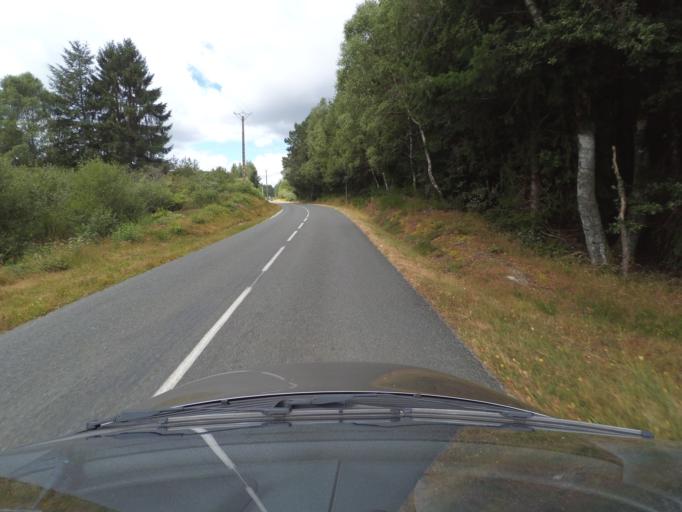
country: FR
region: Limousin
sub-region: Departement de la Haute-Vienne
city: Peyrat-le-Chateau
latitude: 45.8874
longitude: 1.8888
